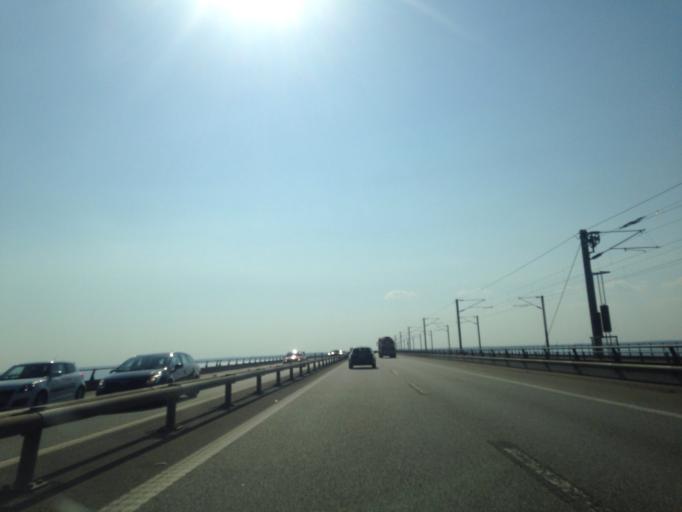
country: DK
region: South Denmark
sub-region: Nyborg Kommune
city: Nyborg
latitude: 55.3147
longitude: 10.9159
